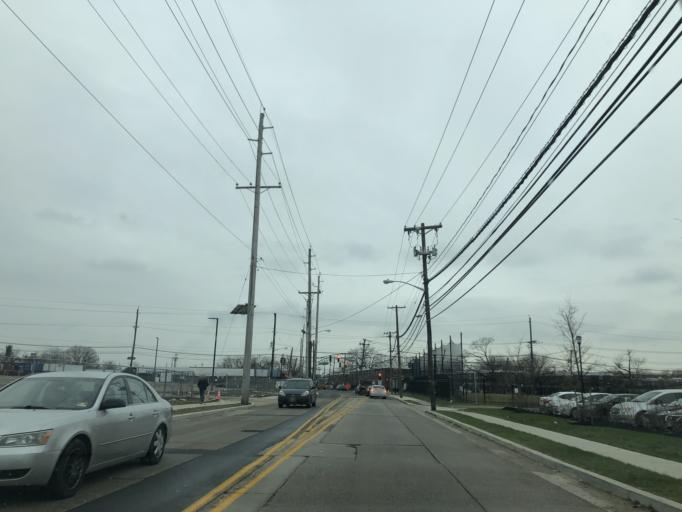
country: US
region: New Jersey
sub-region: Camden County
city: Camden
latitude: 39.9521
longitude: -75.1000
